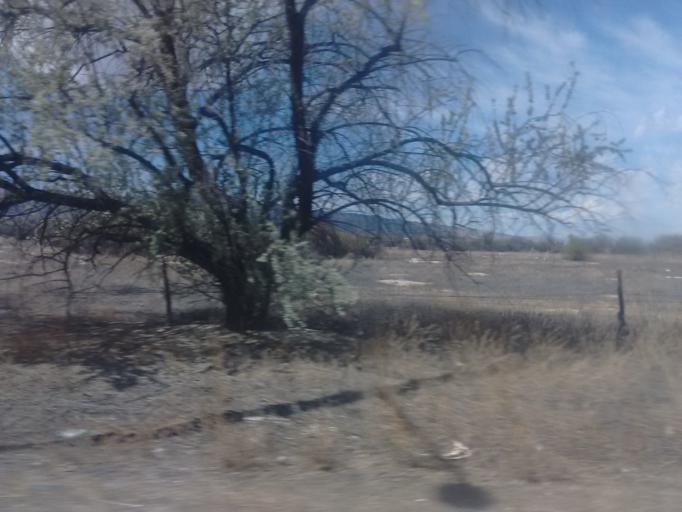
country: US
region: Colorado
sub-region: Mesa County
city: Redlands
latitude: 39.1011
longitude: -108.6082
